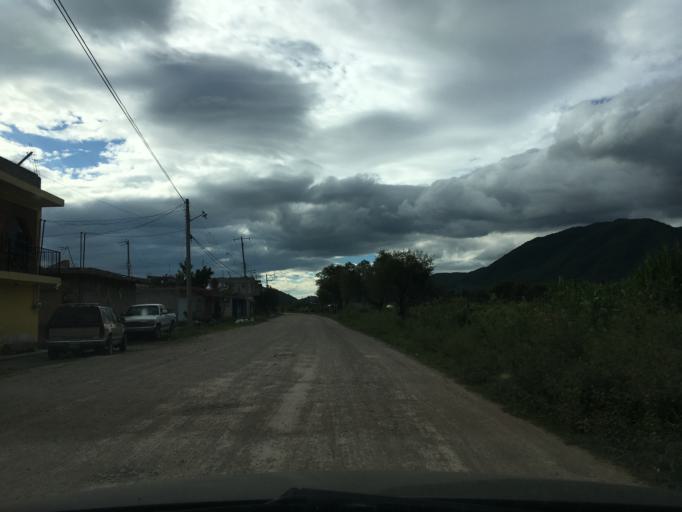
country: MX
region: Guanajuato
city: Iramuco
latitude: 19.9662
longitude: -100.9425
